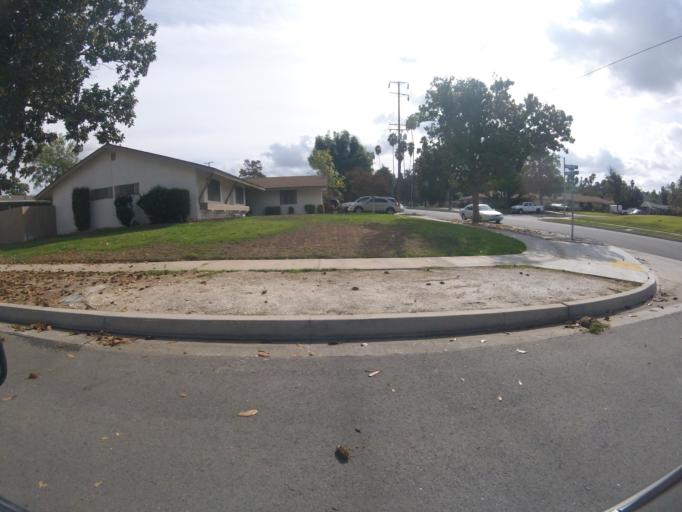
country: US
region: California
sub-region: San Bernardino County
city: Redlands
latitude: 34.0470
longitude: -117.1654
